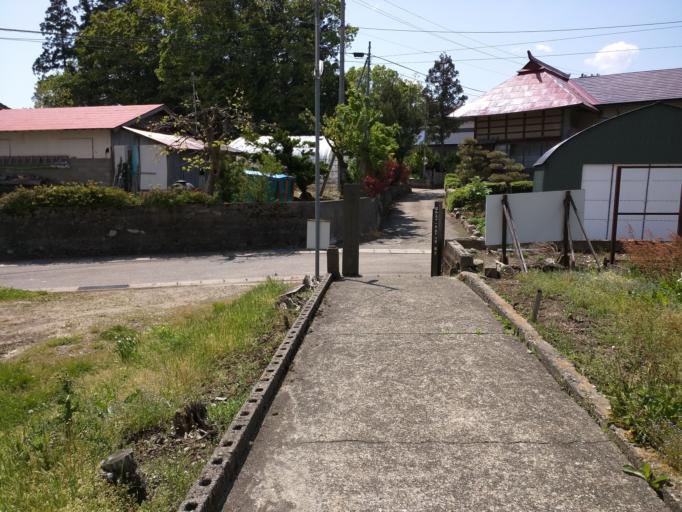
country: JP
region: Fukushima
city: Kitakata
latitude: 37.5924
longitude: 139.8296
